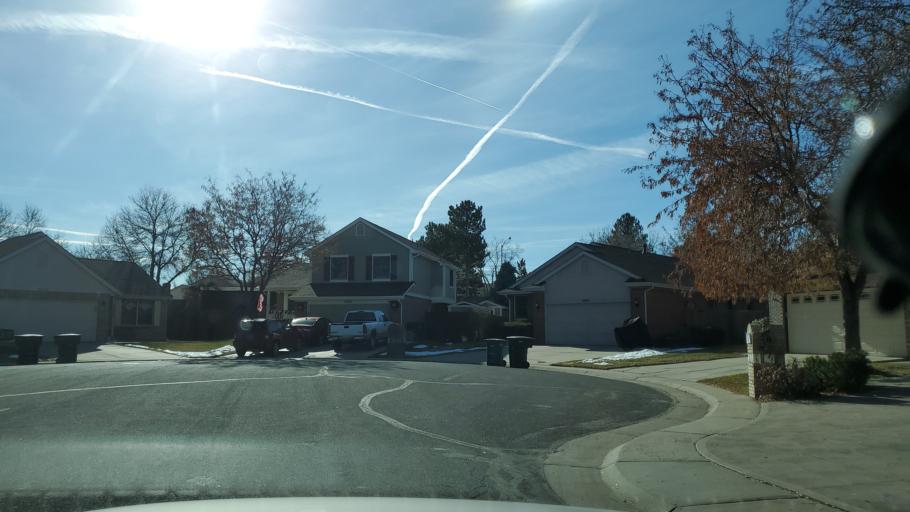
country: US
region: Colorado
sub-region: Adams County
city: Northglenn
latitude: 39.9219
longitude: -104.9546
